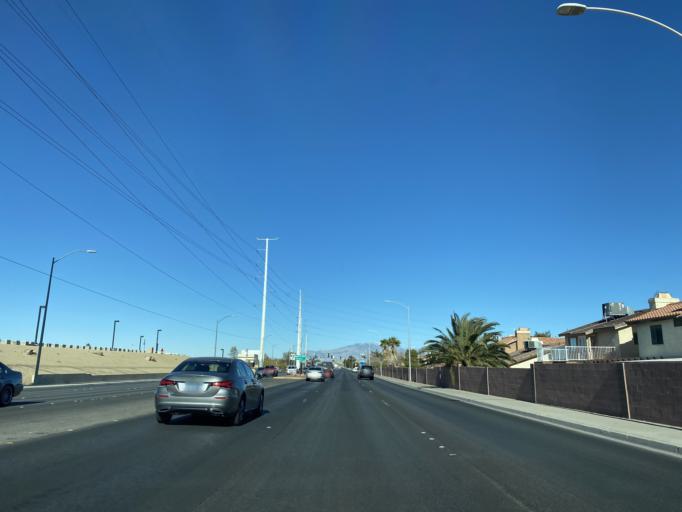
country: US
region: Nevada
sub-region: Clark County
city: Spring Valley
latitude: 36.1714
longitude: -115.2779
